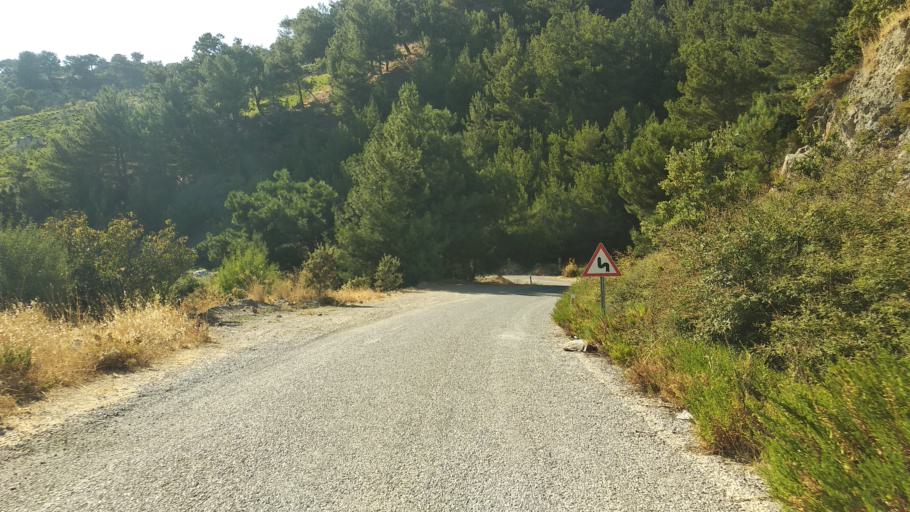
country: TR
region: Izmir
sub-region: Seferihisar
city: Seferhisar
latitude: 38.3222
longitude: 26.9327
